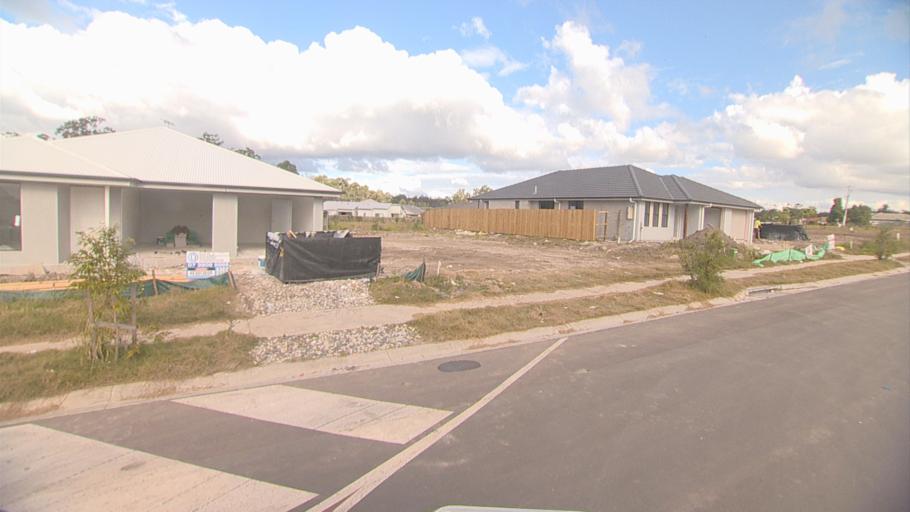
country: AU
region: Queensland
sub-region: Logan
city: Logan Reserve
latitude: -27.6936
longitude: 153.0969
